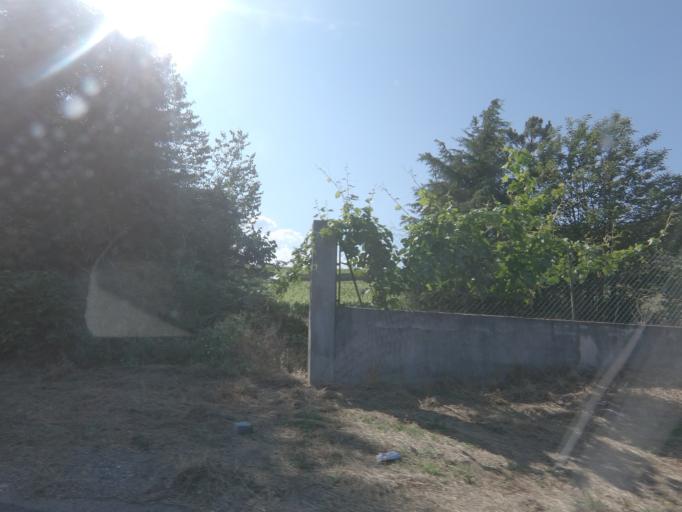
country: PT
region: Vila Real
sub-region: Sabrosa
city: Sabrosa
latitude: 41.2573
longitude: -7.5842
